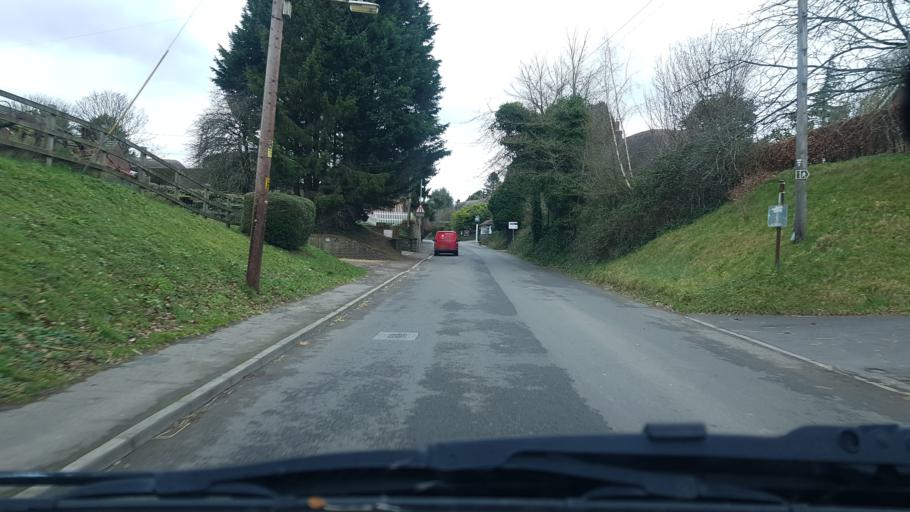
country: GB
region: England
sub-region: Wiltshire
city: Burbage
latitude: 51.3503
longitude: -1.6708
